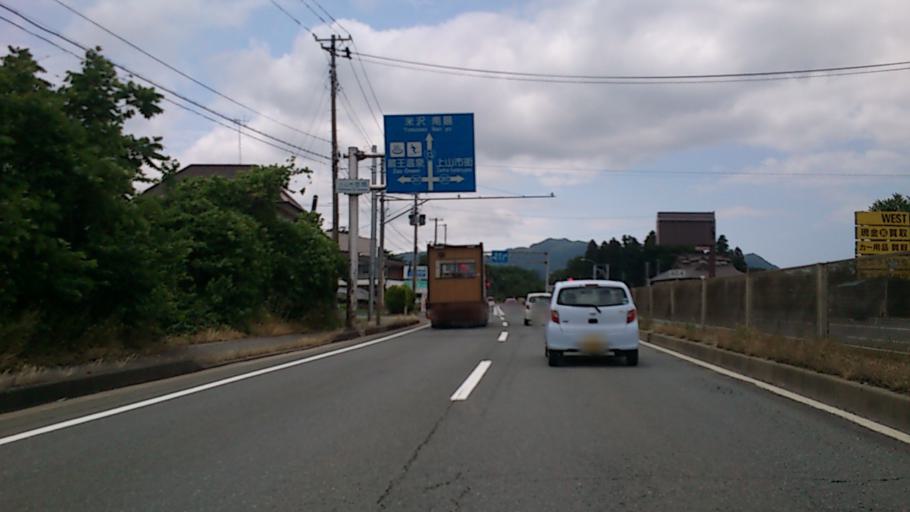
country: JP
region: Yamagata
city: Kaminoyama
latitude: 38.1850
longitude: 140.3098
